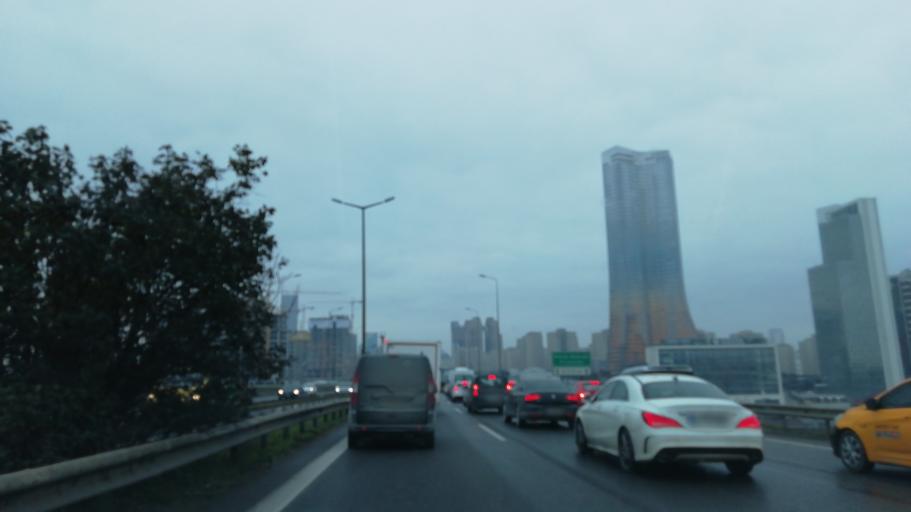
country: TR
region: Istanbul
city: Umraniye
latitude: 41.0053
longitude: 29.1001
